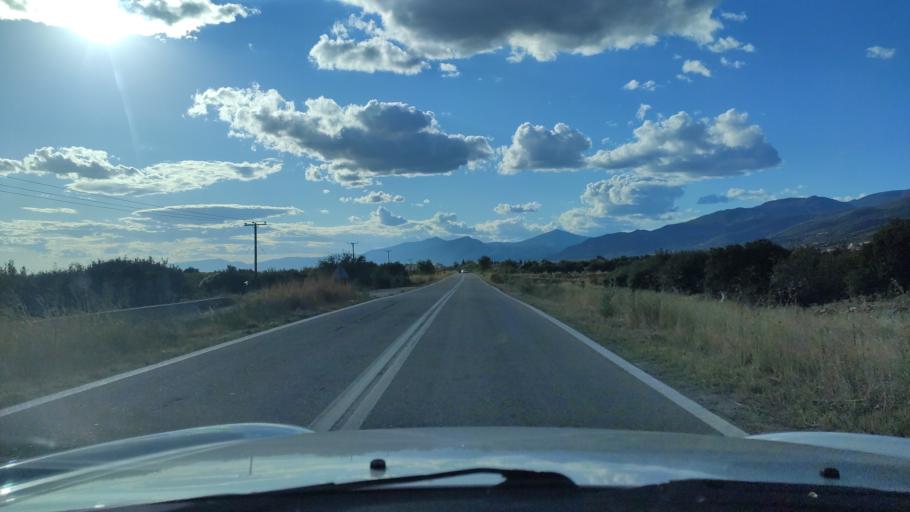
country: GR
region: East Macedonia and Thrace
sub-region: Nomos Xanthis
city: Selero
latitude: 41.1218
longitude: 25.0744
